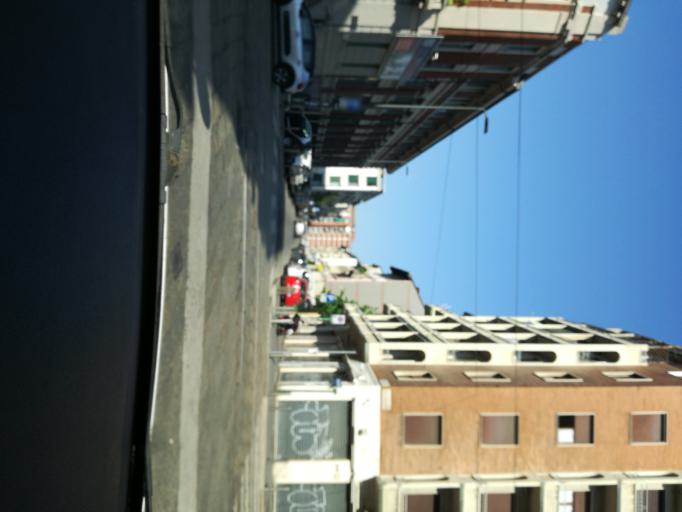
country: IT
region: Lombardy
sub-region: Citta metropolitana di Milano
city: Milano
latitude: 45.4362
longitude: 9.1784
